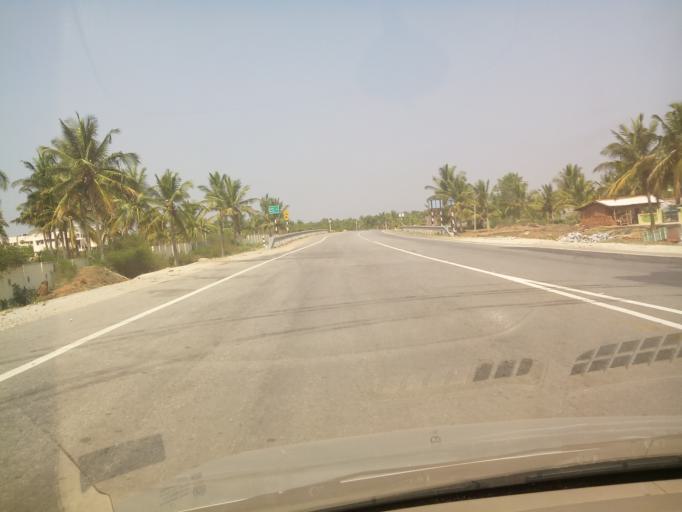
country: IN
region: Karnataka
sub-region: Hassan
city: Channarayapatna
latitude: 12.9075
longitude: 76.4245
